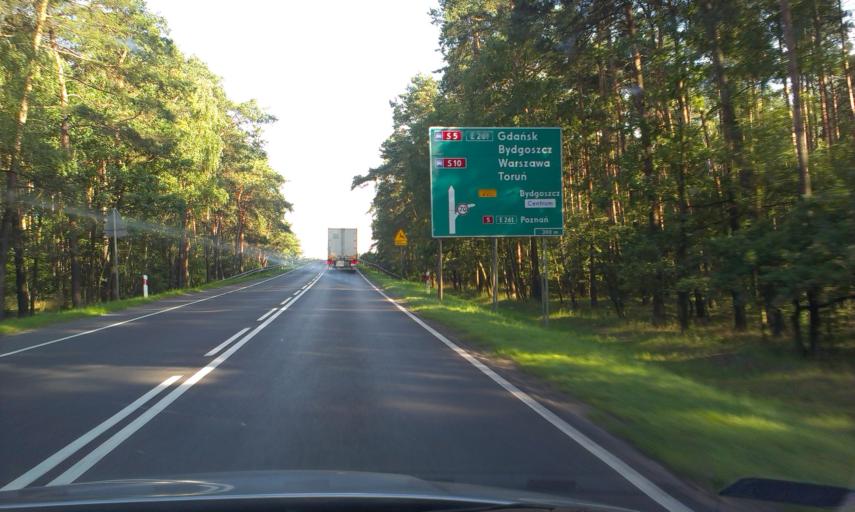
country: PL
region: Kujawsko-Pomorskie
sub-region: Powiat bydgoski
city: Biale Blota
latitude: 53.1028
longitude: 17.8892
